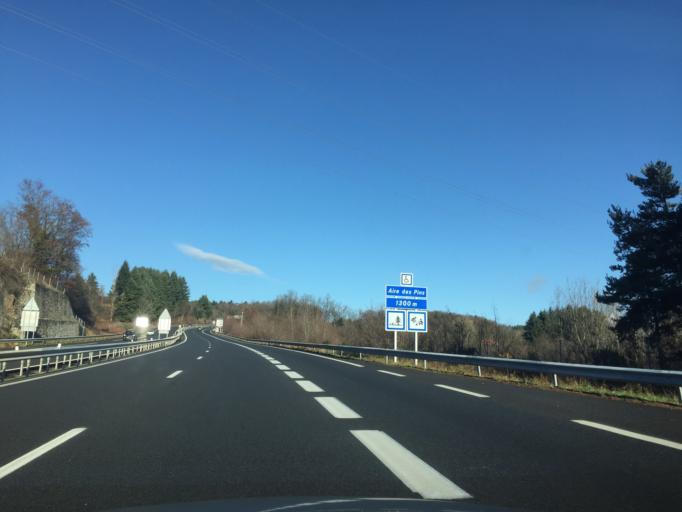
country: FR
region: Auvergne
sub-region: Departement du Puy-de-Dome
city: Thiers
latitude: 45.8688
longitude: 3.5601
